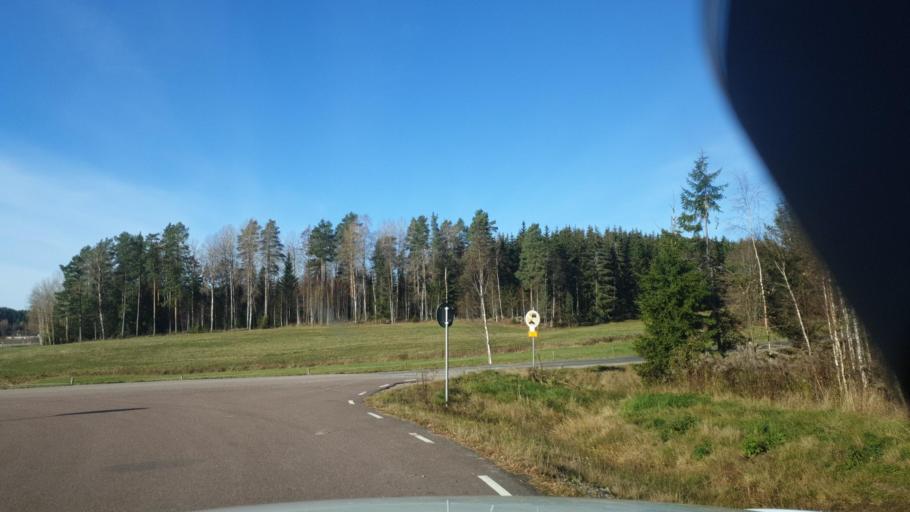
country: SE
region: Vaermland
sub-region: Arvika Kommun
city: Arvika
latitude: 59.6538
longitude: 12.6571
